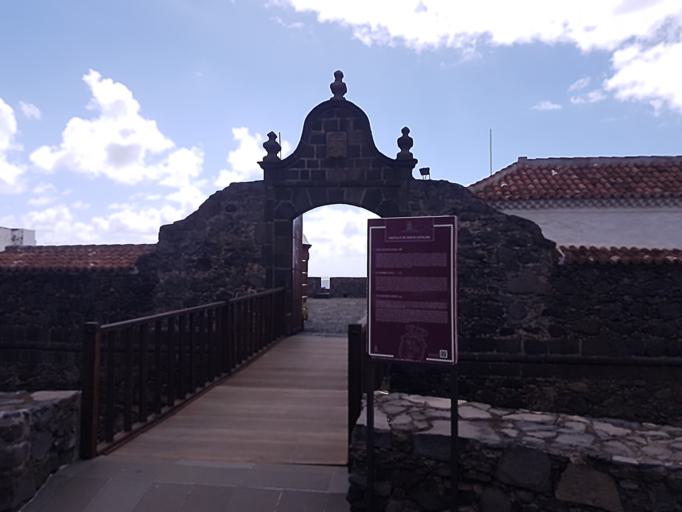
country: ES
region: Canary Islands
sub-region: Provincia de Santa Cruz de Tenerife
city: Santa Cruz de la Palma
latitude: 28.6871
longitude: -17.7609
